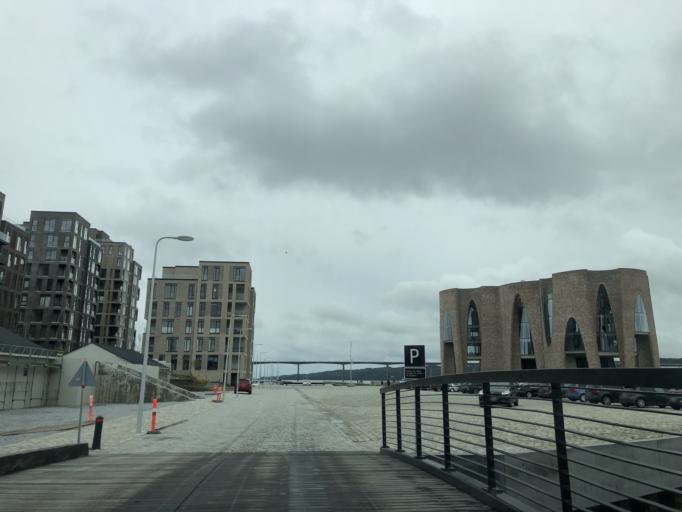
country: DK
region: South Denmark
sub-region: Vejle Kommune
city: Vejle
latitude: 55.7068
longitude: 9.5531
